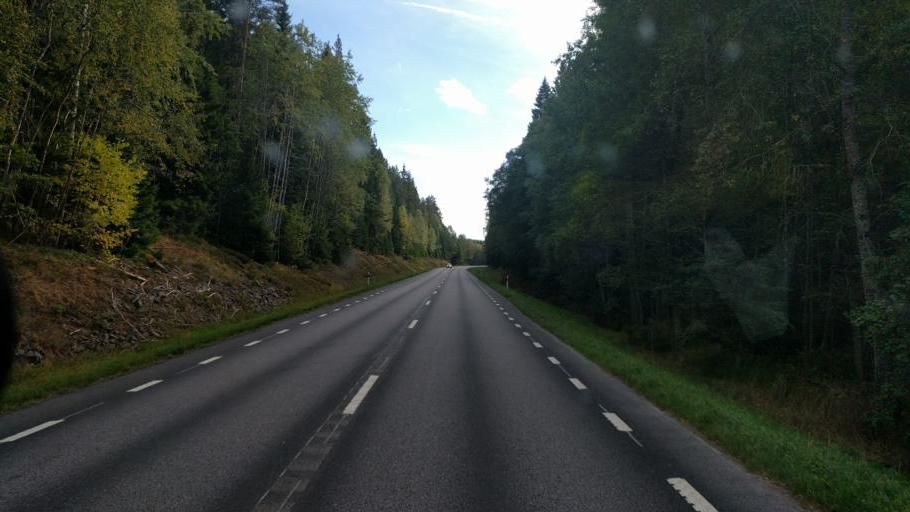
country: SE
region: OEstergoetland
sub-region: Kinda Kommun
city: Kisa
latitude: 57.9531
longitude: 15.6621
